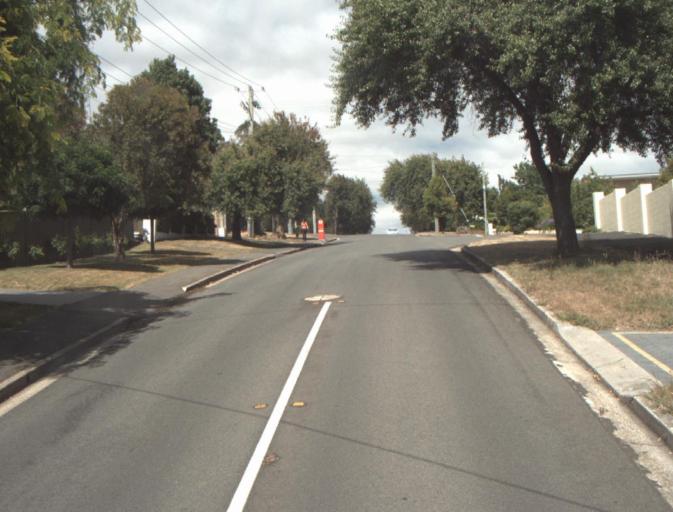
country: AU
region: Tasmania
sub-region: Launceston
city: West Launceston
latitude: -41.4531
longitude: 147.1264
